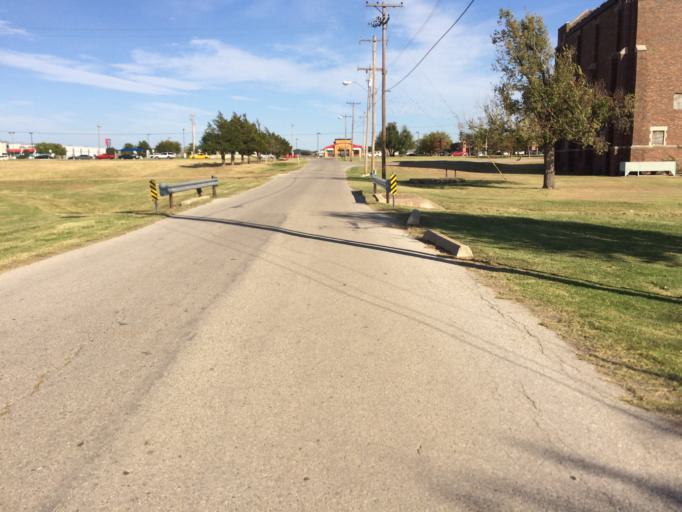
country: US
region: Oklahoma
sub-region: Cleveland County
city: Norman
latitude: 35.2292
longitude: -97.4253
